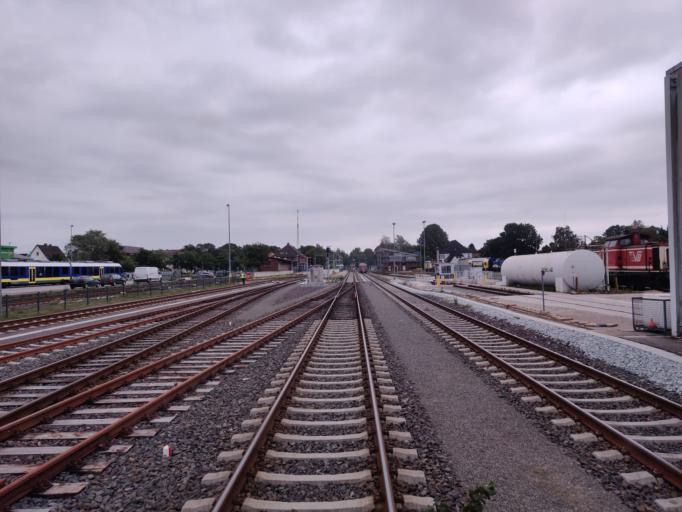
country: DE
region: Lower Saxony
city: Bremervorde
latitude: 53.4839
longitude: 9.1373
